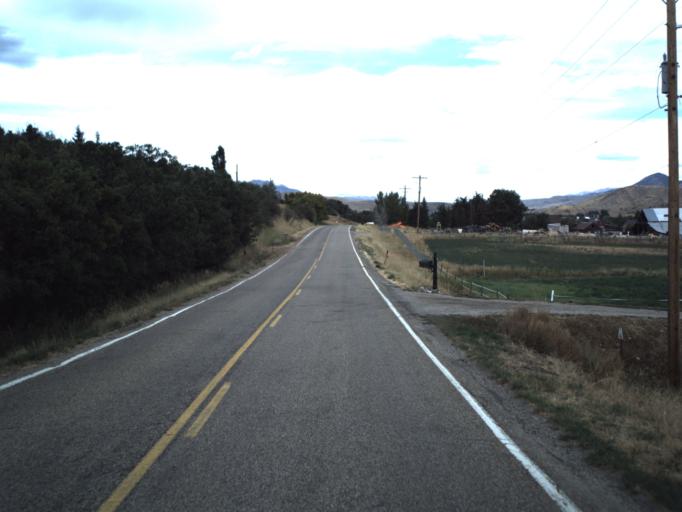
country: US
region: Utah
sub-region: Morgan County
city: Morgan
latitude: 40.9551
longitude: -111.6650
